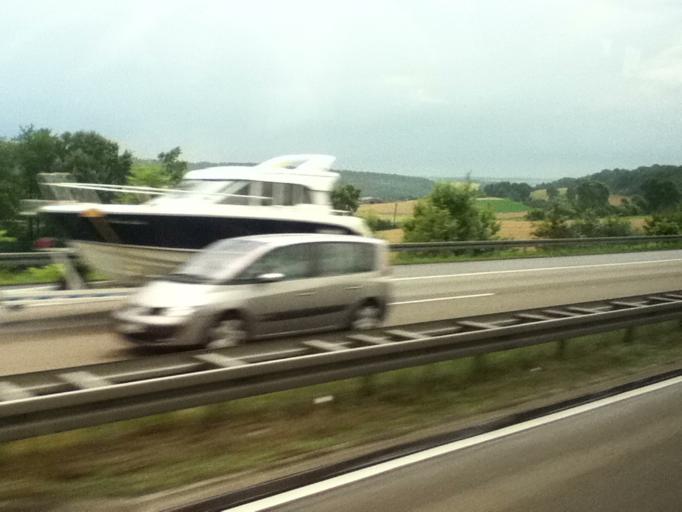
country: DE
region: Hesse
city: Kirtorf
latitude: 50.7156
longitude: 9.1216
